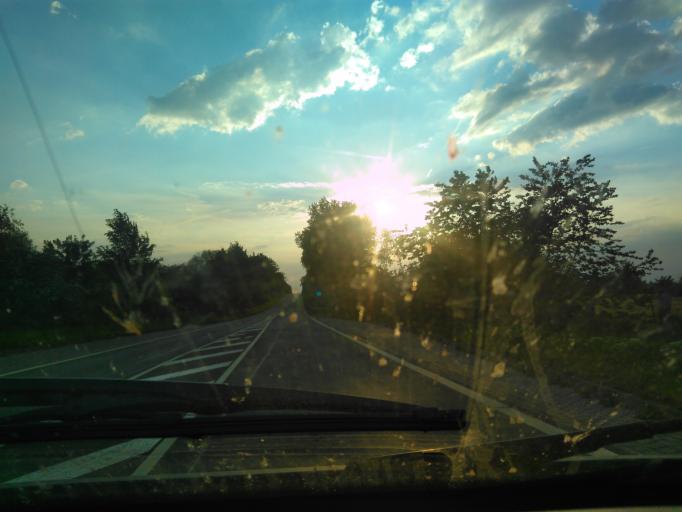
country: DE
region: Saxony-Anhalt
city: Stossen
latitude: 51.1101
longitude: 11.9271
